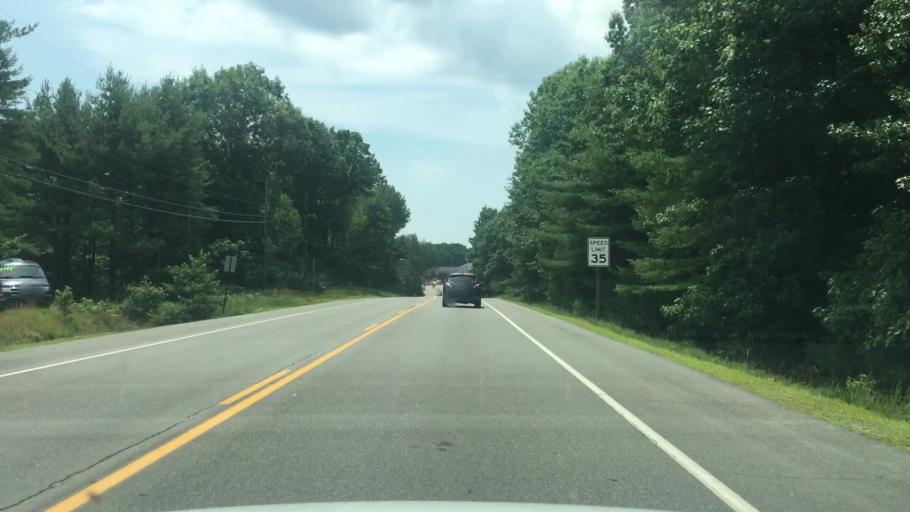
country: US
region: New Hampshire
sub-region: Strafford County
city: Rochester
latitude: 43.3396
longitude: -70.9382
